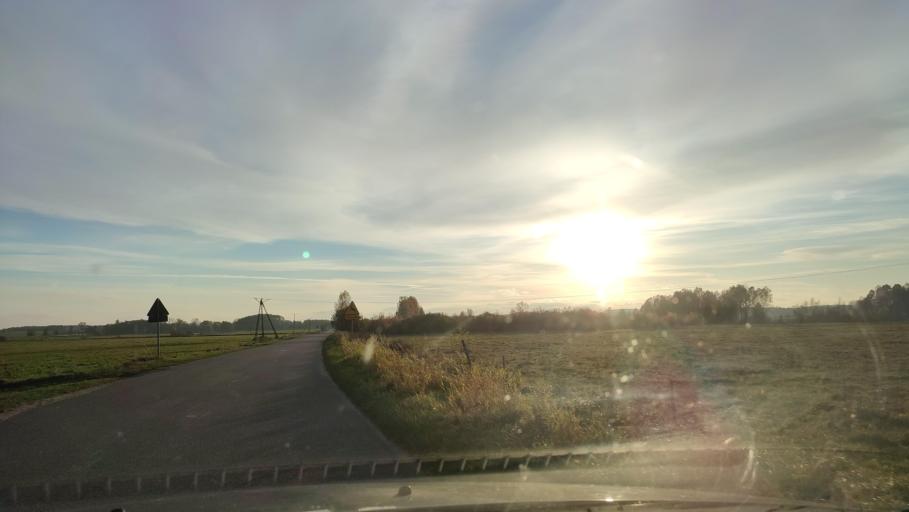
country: PL
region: Masovian Voivodeship
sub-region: Powiat mlawski
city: Dzierzgowo
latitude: 53.2878
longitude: 20.6593
